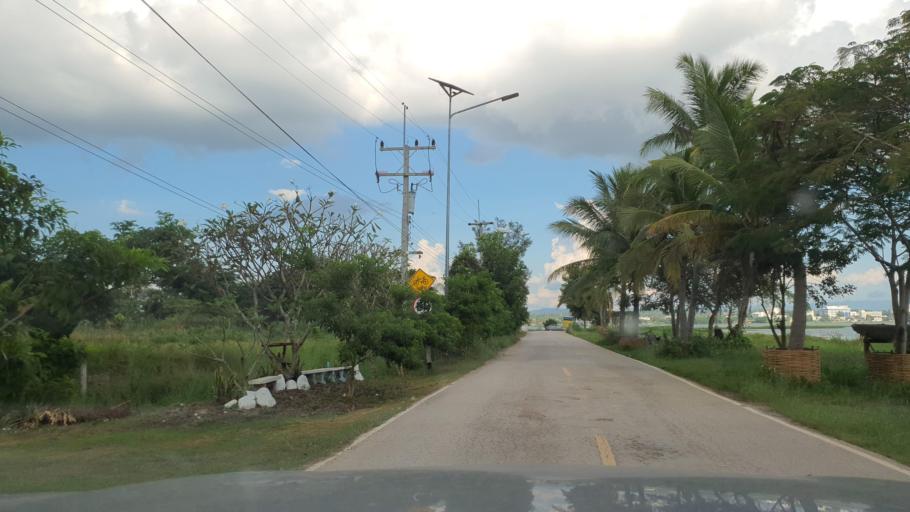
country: TH
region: Phayao
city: Phayao
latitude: 19.1929
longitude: 99.8586
